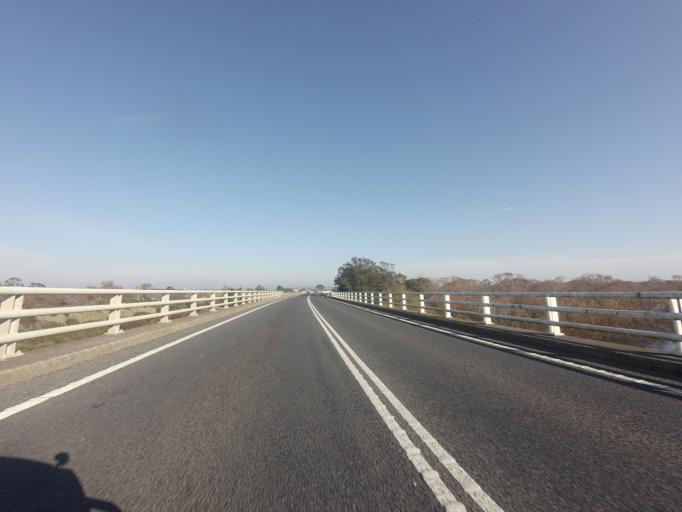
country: AU
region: Tasmania
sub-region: Northern Midlands
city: Longford
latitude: -41.5846
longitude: 147.1270
